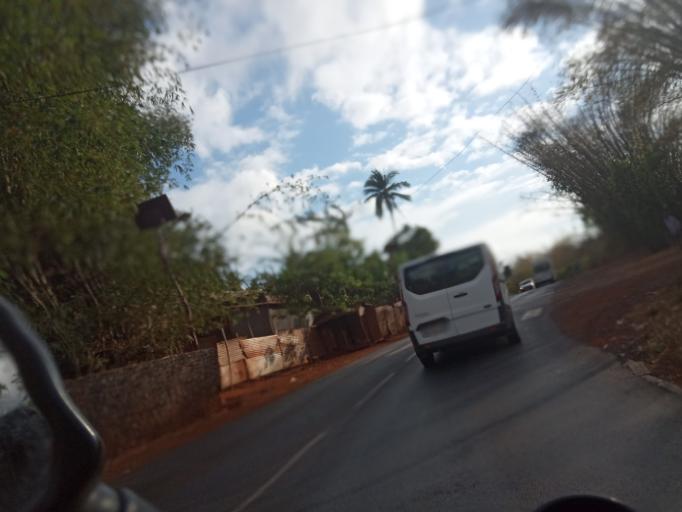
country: YT
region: Dembeni
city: Dembeni
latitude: -12.8689
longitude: 45.1980
